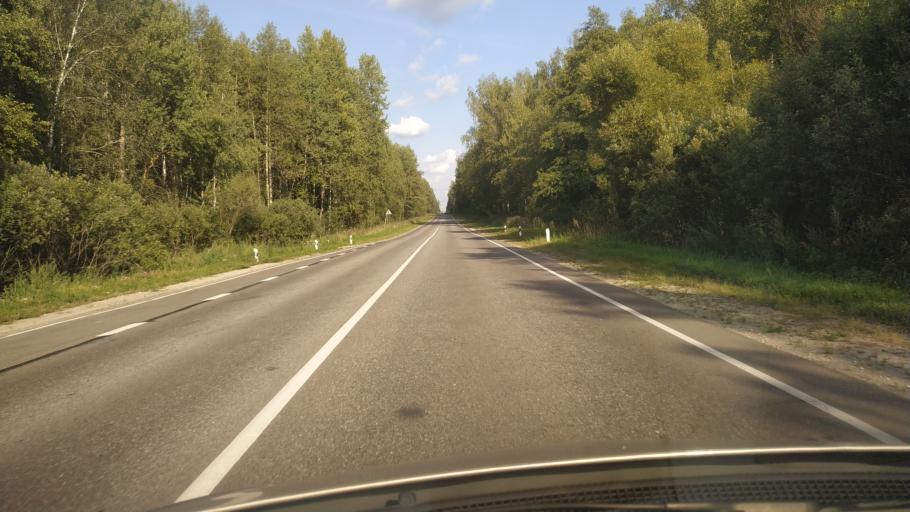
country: RU
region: Moskovskaya
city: Vereya
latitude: 55.7027
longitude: 39.1887
